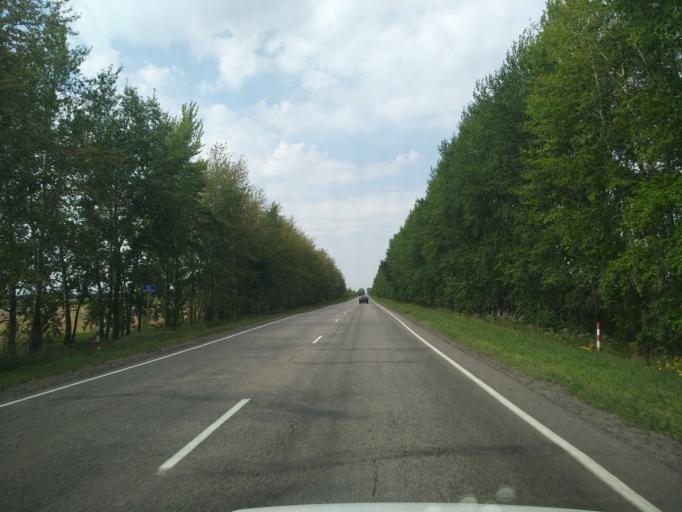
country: RU
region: Voronezj
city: Pereleshino
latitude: 51.7187
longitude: 40.0231
